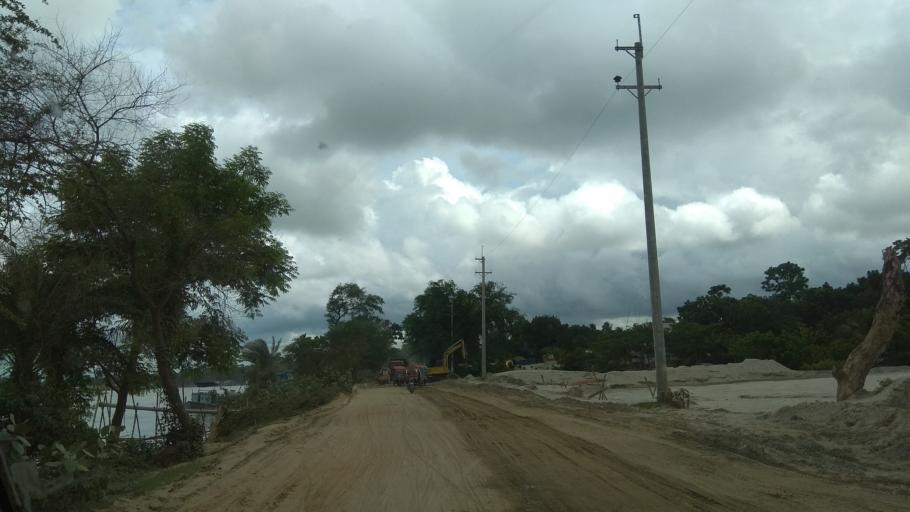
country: BD
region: Khulna
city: Kalia
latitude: 23.2041
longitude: 89.6983
